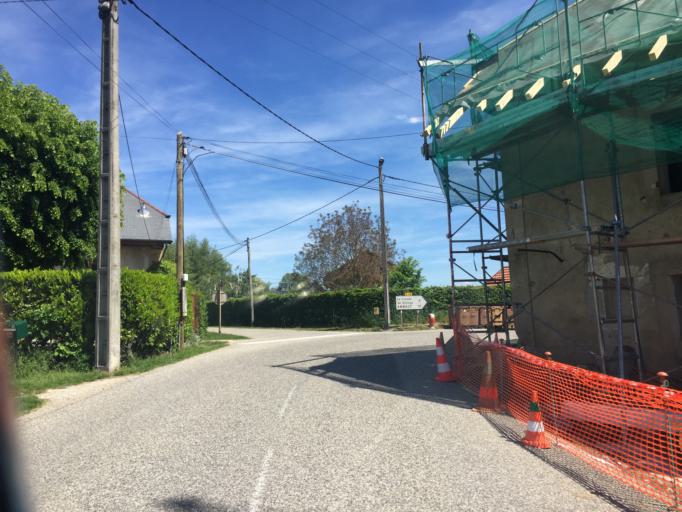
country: FR
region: Rhone-Alpes
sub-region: Departement de la Haute-Savoie
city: Chilly
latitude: 45.9485
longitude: 5.9715
